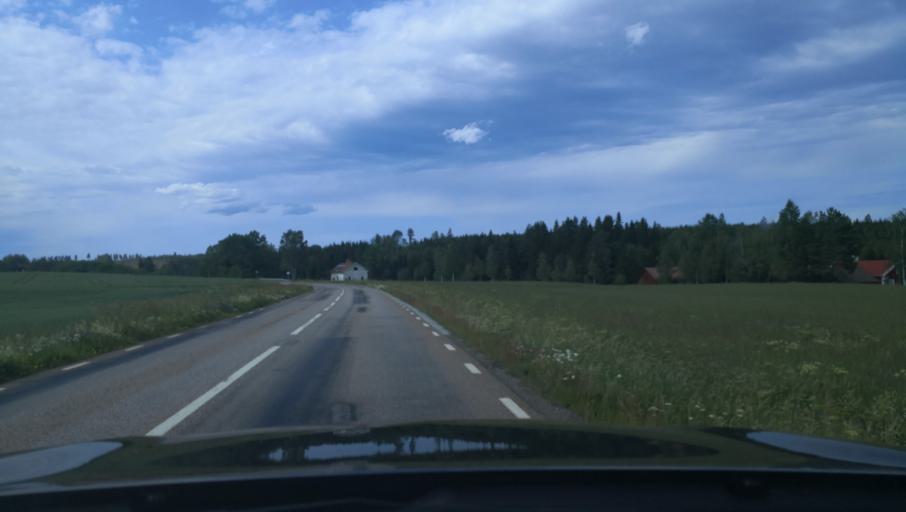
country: SE
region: Dalarna
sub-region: Avesta Kommun
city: Avesta
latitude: 59.9893
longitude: 16.1155
